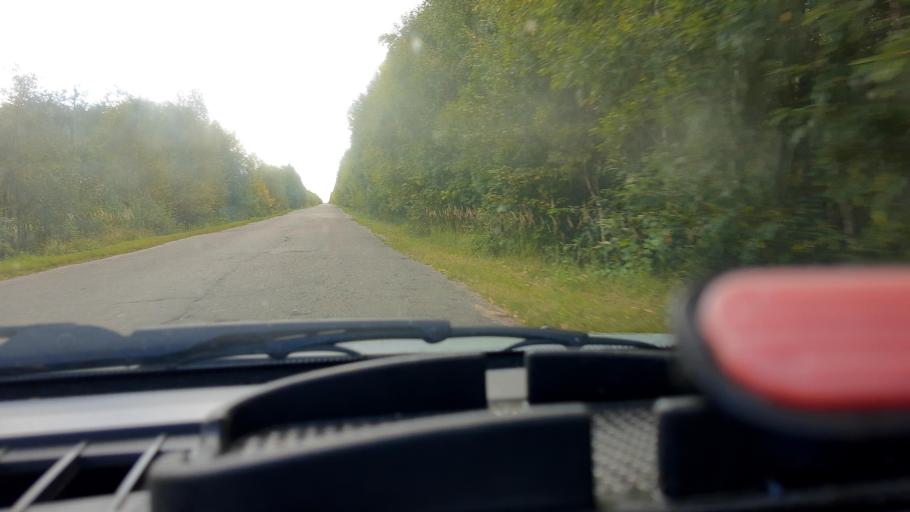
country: RU
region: Mariy-El
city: Kilemary
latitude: 56.9058
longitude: 46.7359
